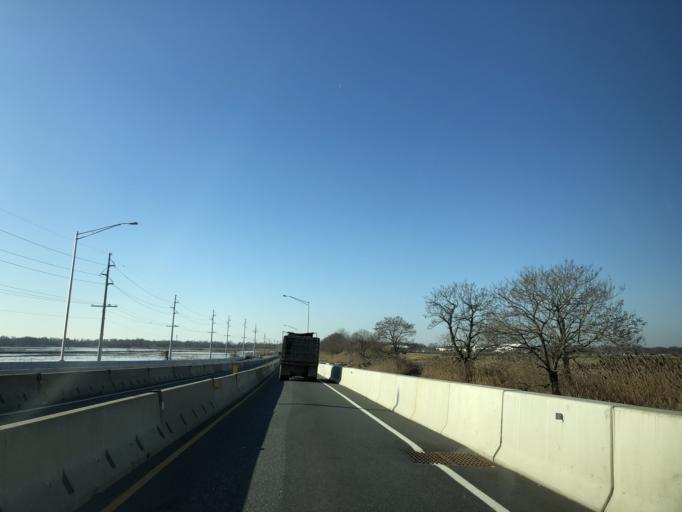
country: US
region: New Jersey
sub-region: Gloucester County
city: Beckett
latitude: 39.8005
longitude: -75.3573
